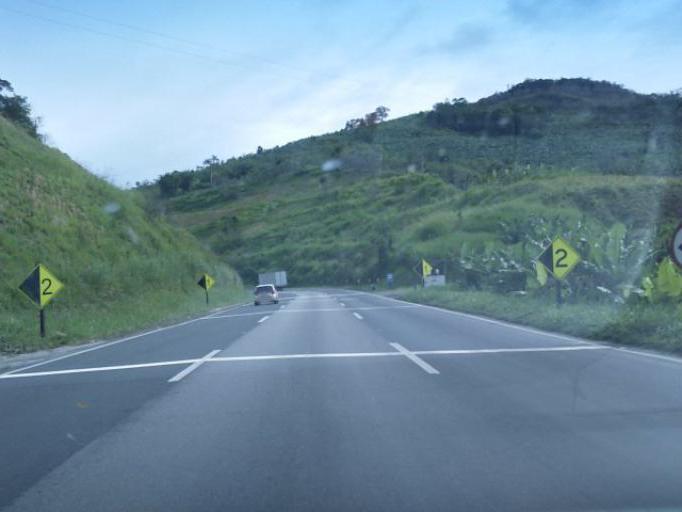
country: BR
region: Sao Paulo
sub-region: Cajati
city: Cajati
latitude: -24.8644
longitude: -48.2186
